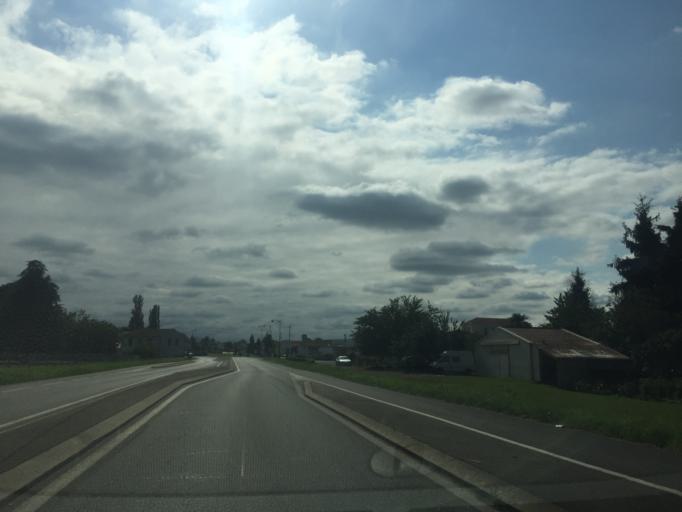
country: FR
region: Midi-Pyrenees
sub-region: Departement de la Haute-Garonne
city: Saint-Gaudens
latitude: 43.0966
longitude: 0.7048
